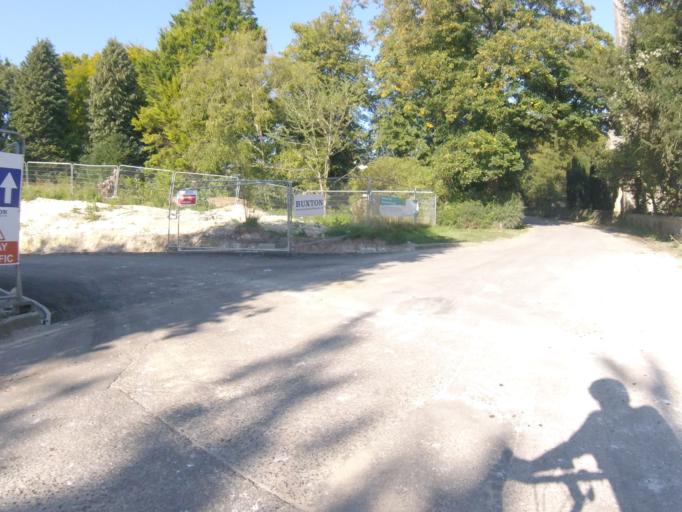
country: GB
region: England
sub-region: Brighton and Hove
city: Brighton
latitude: 50.8702
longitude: -0.1025
